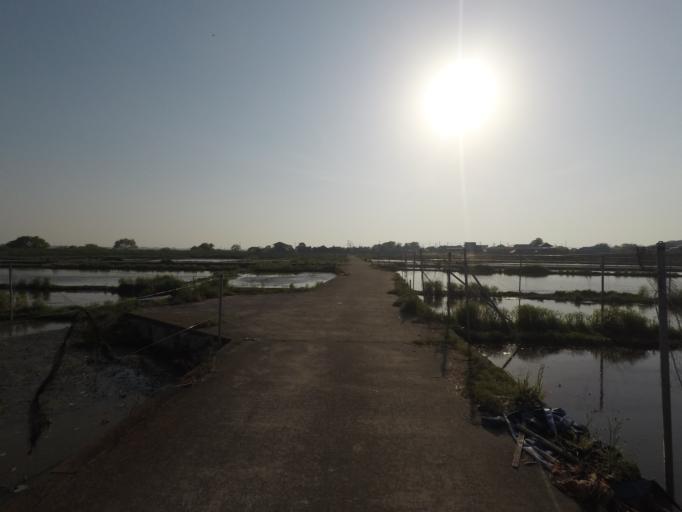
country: JP
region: Ibaraki
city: Ami
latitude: 36.0695
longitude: 140.2592
